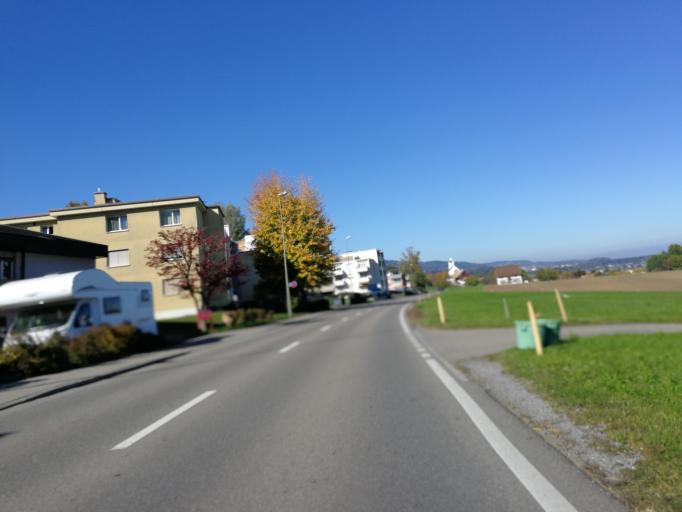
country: CH
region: Zurich
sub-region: Bezirk Meilen
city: Oetwil am See
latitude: 47.2664
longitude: 8.7289
